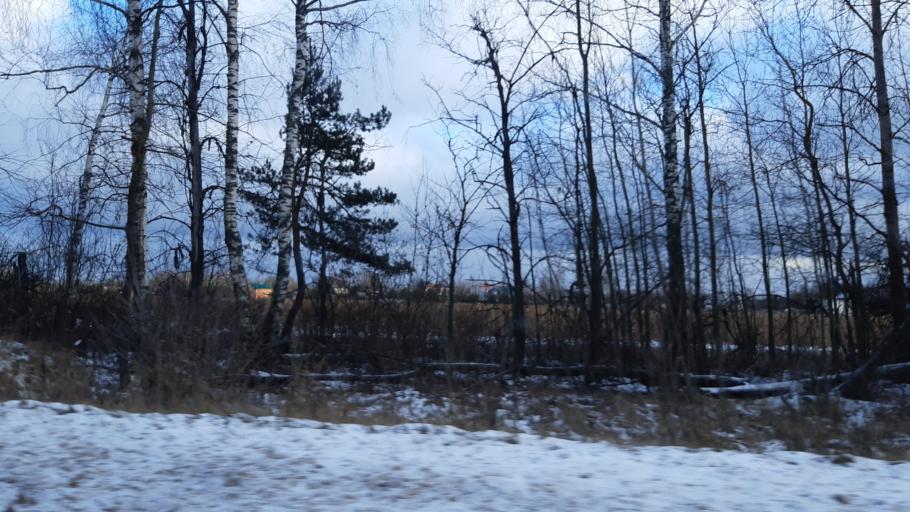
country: RU
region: Moskovskaya
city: Noginsk-9
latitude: 56.0088
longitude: 38.5591
